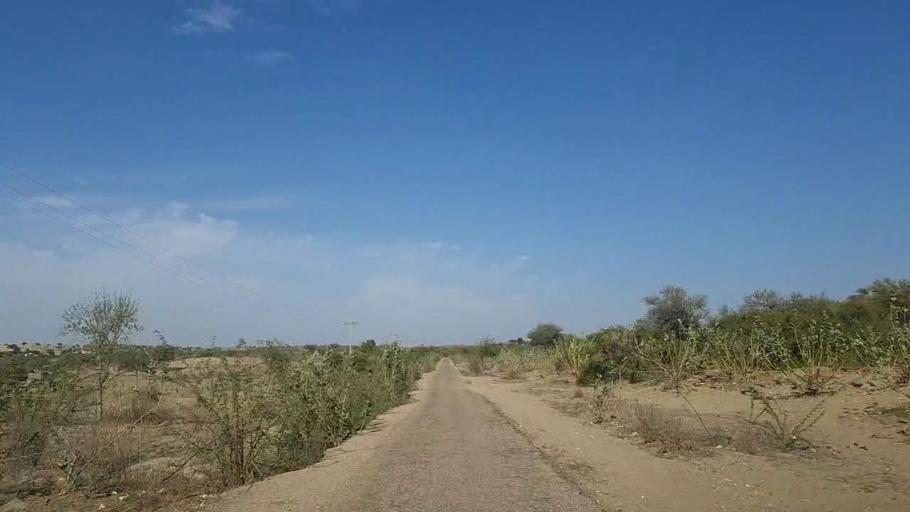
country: PK
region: Sindh
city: Naukot
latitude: 24.8273
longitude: 69.5448
